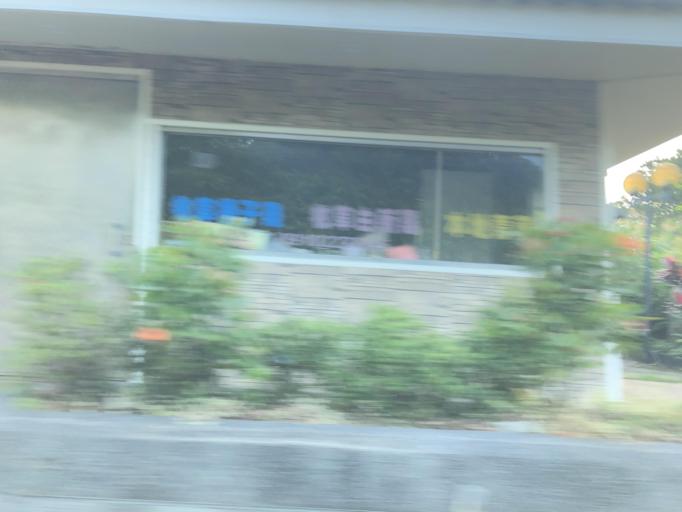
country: TW
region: Taiwan
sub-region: Keelung
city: Keelung
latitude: 25.2004
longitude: 121.6463
